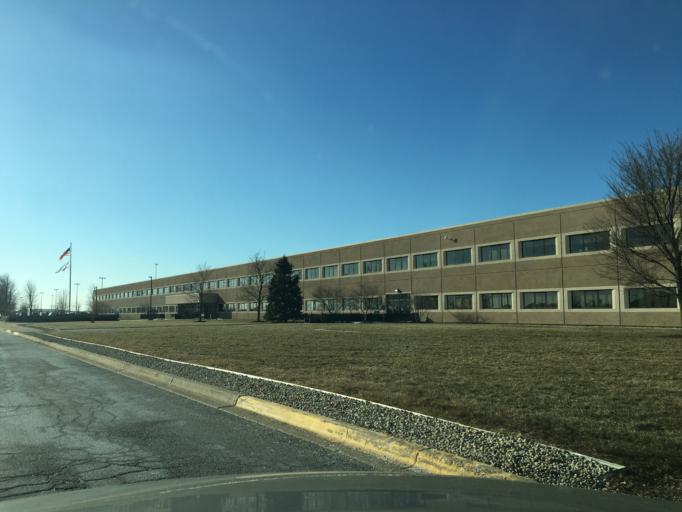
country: US
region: Illinois
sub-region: Cook County
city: Rosemont
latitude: 41.9958
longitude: -87.8871
